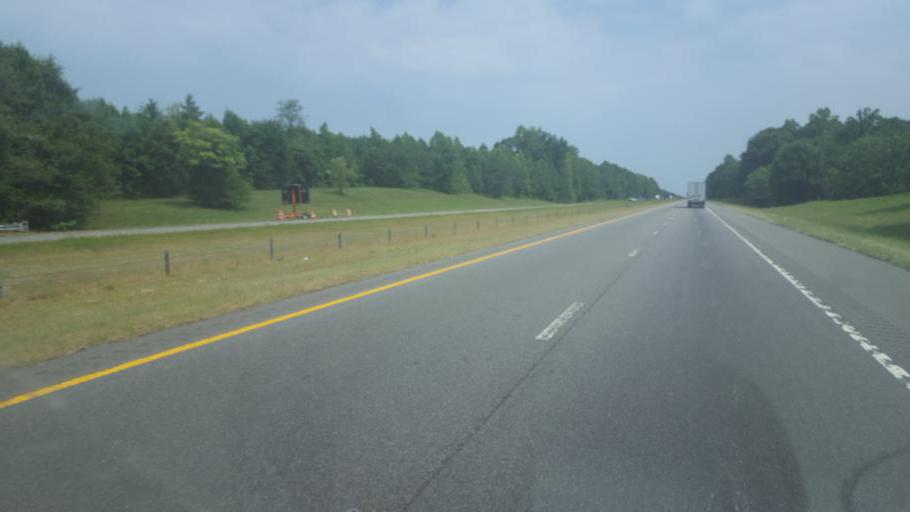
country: US
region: North Carolina
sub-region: Iredell County
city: Statesville
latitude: 35.9450
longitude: -80.8517
